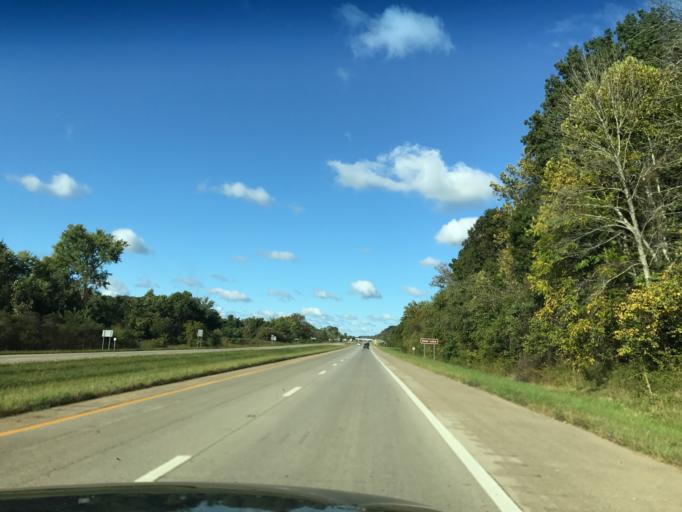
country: US
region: Ohio
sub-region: Athens County
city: Athens
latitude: 39.3343
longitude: -82.0127
